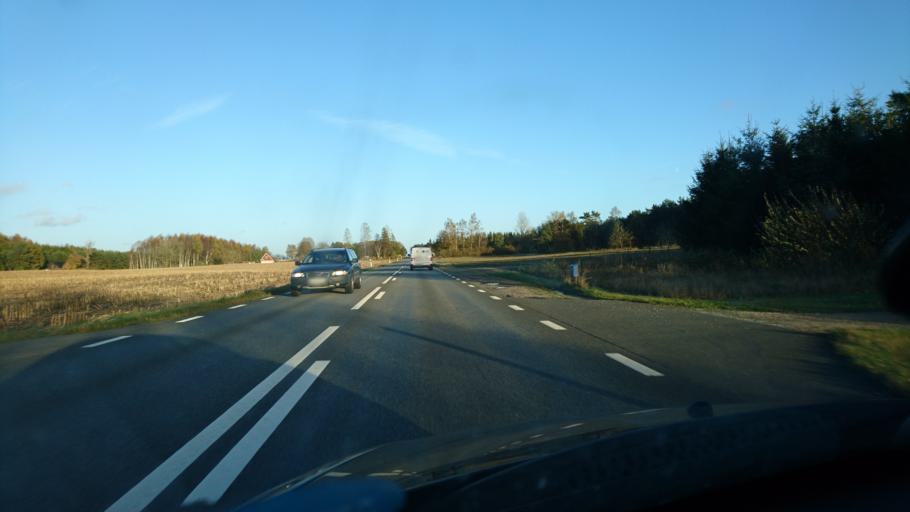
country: SE
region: Skane
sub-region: Tomelilla Kommun
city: Tomelilla
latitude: 55.5534
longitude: 14.0823
